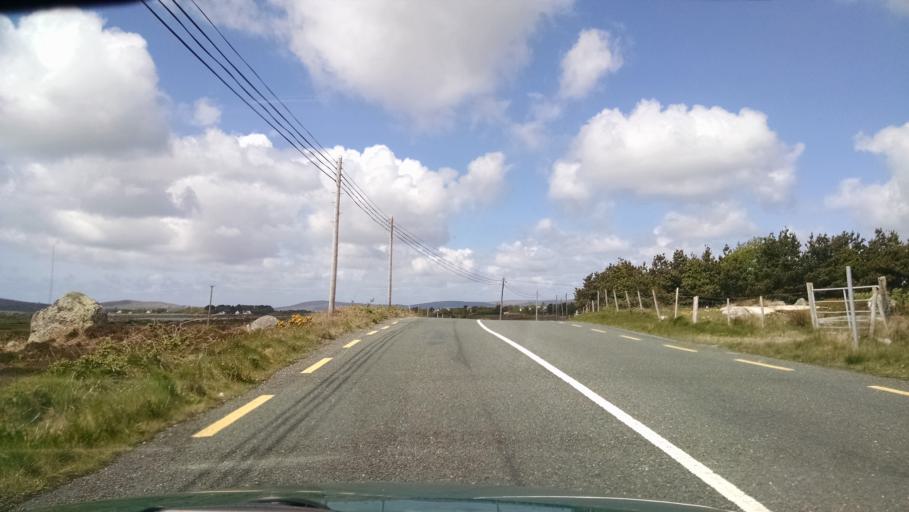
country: IE
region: Connaught
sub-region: County Galway
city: Oughterard
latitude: 53.3117
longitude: -9.6033
